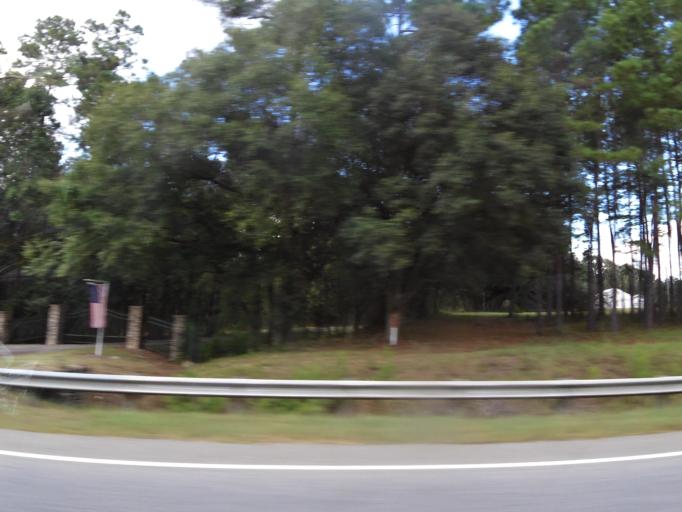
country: US
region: Georgia
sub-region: Brooks County
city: Quitman
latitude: 30.7875
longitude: -83.5112
